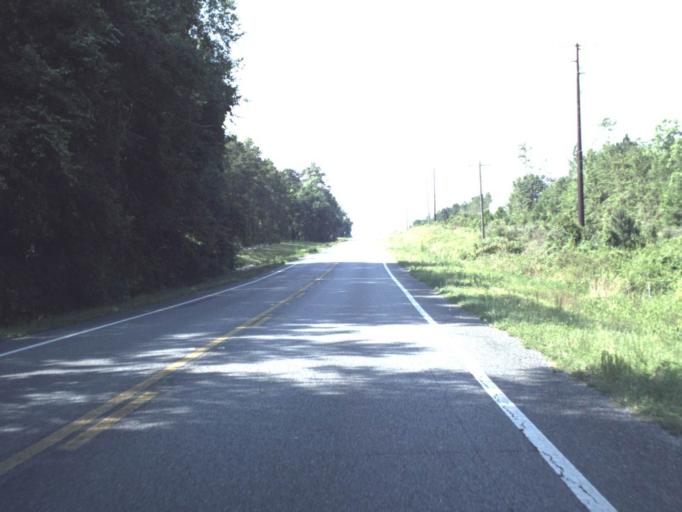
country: US
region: Florida
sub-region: Clay County
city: Middleburg
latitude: 30.0231
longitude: -81.8976
